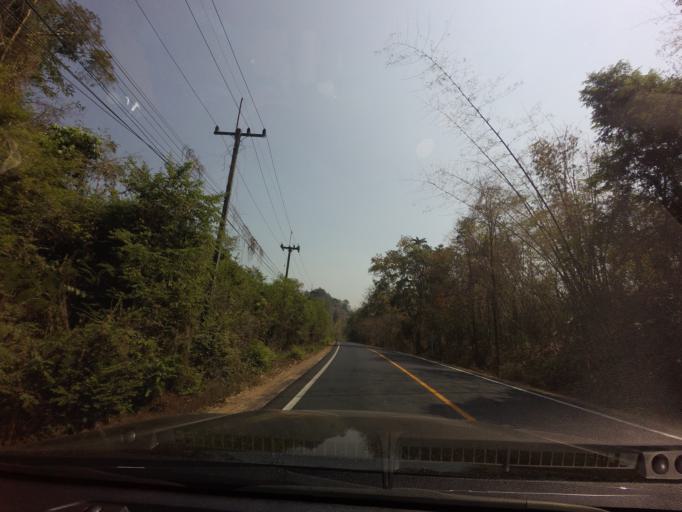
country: TH
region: Kanchanaburi
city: Thong Pha Phum
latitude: 14.7804
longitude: 98.5794
